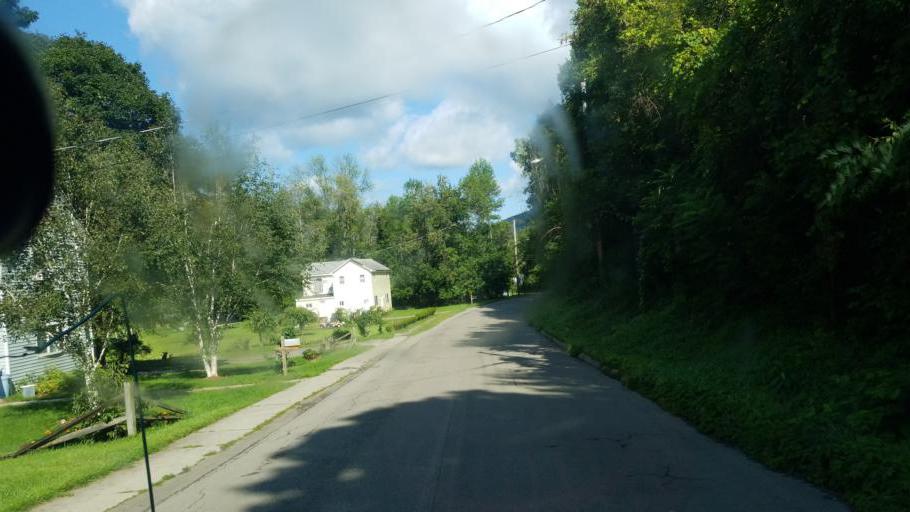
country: US
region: New York
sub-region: Steuben County
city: Canisteo
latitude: 42.2808
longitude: -77.6034
